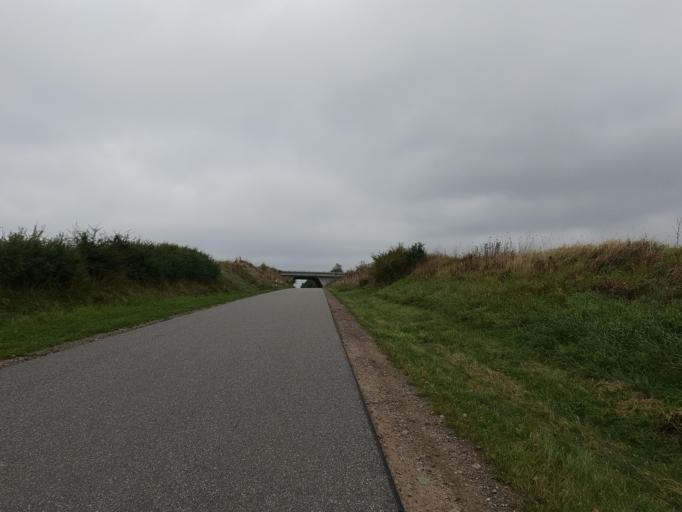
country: DE
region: Schleswig-Holstein
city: Heiligenhafen
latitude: 54.3607
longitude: 10.9853
